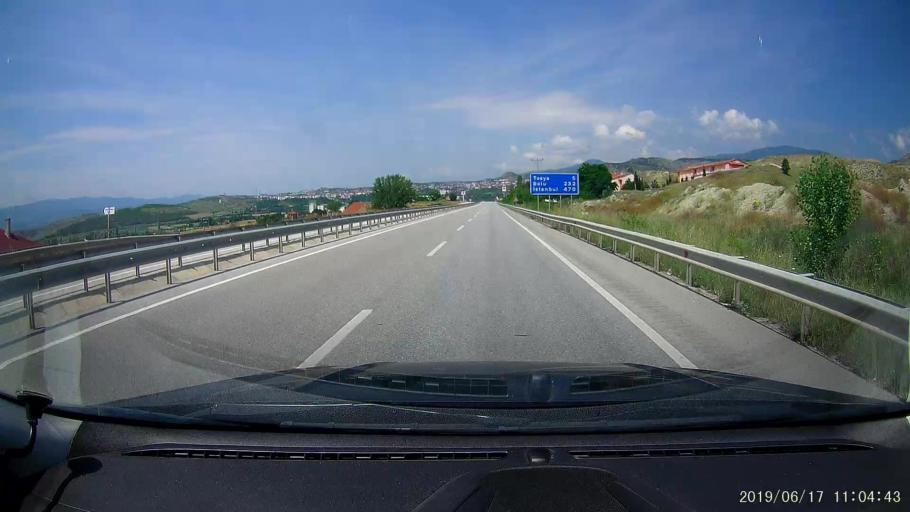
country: TR
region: Kastamonu
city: Tosya
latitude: 41.0195
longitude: 34.0883
